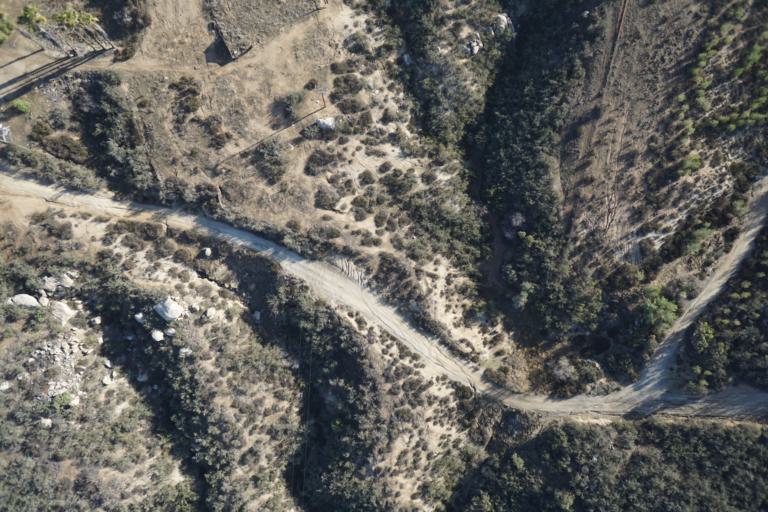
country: US
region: California
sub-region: Riverside County
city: East Hemet
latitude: 33.6146
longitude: -116.9112
